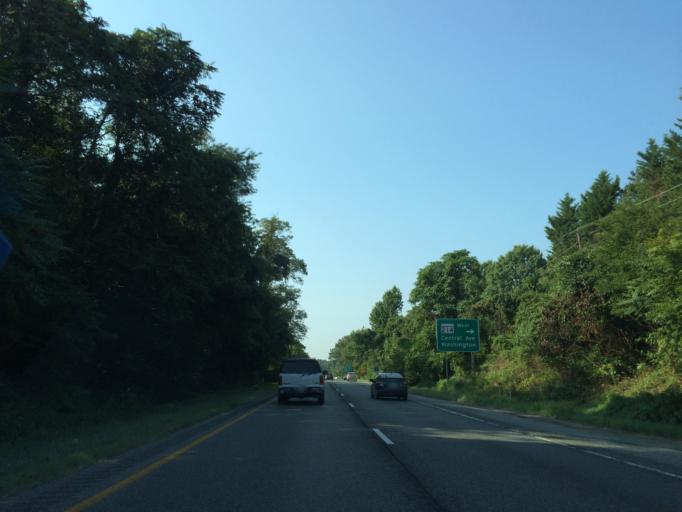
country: US
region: Maryland
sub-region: Prince George's County
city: Mitchellville
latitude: 38.9024
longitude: -76.7199
